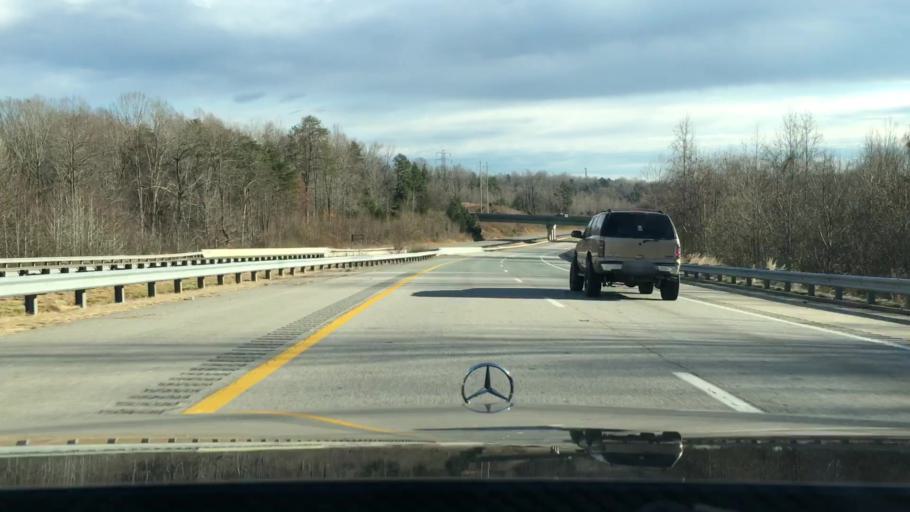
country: US
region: Virginia
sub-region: City of Danville
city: Danville
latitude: 36.6109
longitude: -79.3605
